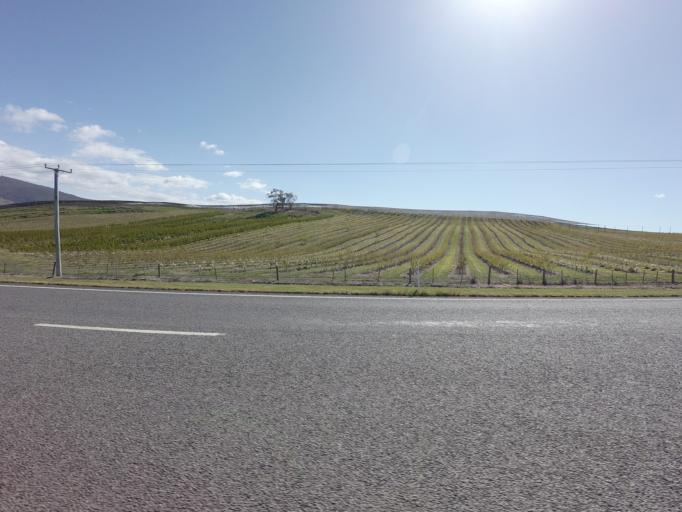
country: AU
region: Tasmania
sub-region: Derwent Valley
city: New Norfolk
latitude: -42.7130
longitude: 146.9469
